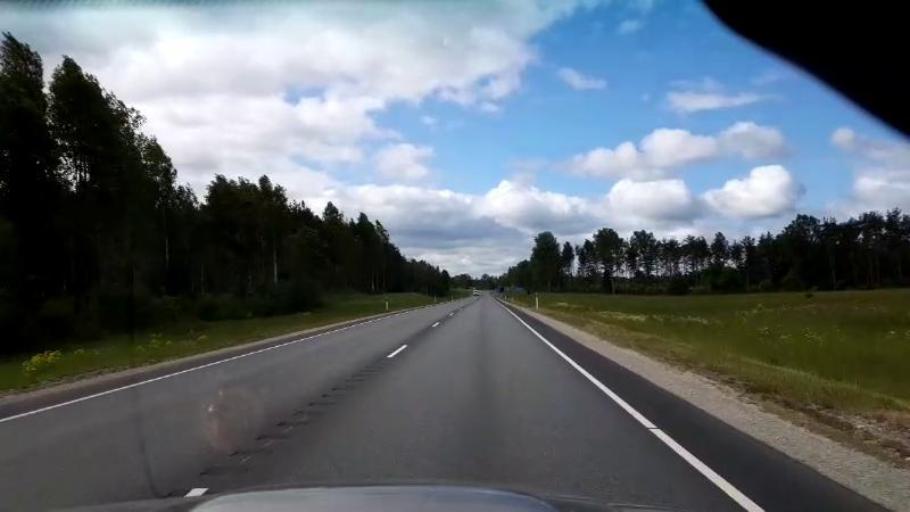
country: EE
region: Harju
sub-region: Nissi vald
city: Riisipere
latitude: 59.0818
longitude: 24.4574
